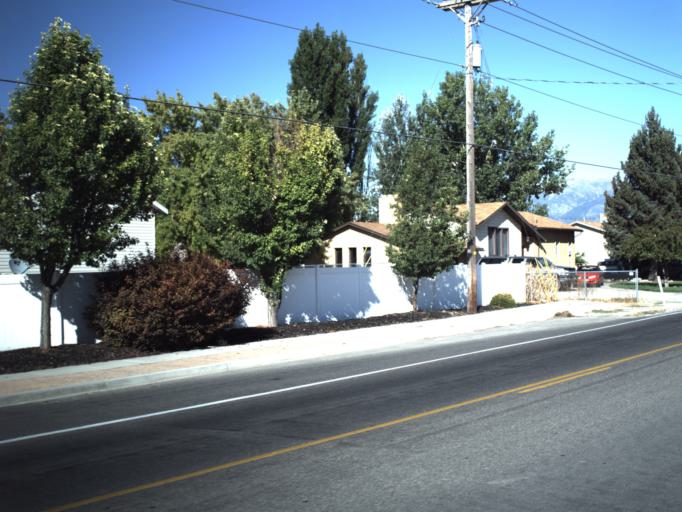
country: US
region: Utah
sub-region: Davis County
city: West Point
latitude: 41.1398
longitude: -112.0746
